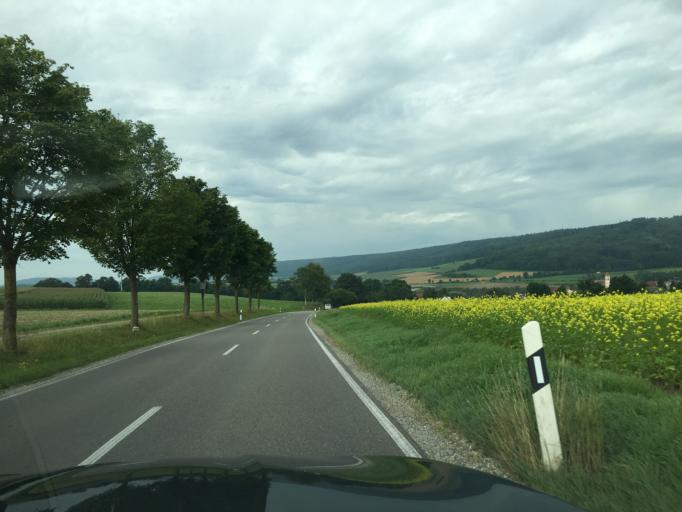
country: DE
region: Baden-Wuerttemberg
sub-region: Tuebingen Region
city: Emeringen
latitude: 48.2020
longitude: 9.5132
